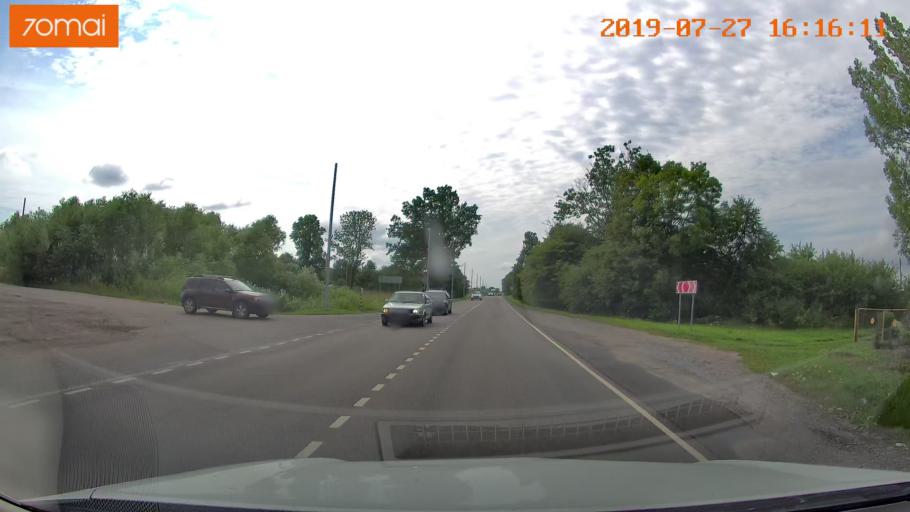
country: RU
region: Kaliningrad
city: Chernyakhovsk
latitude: 54.6239
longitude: 21.5779
